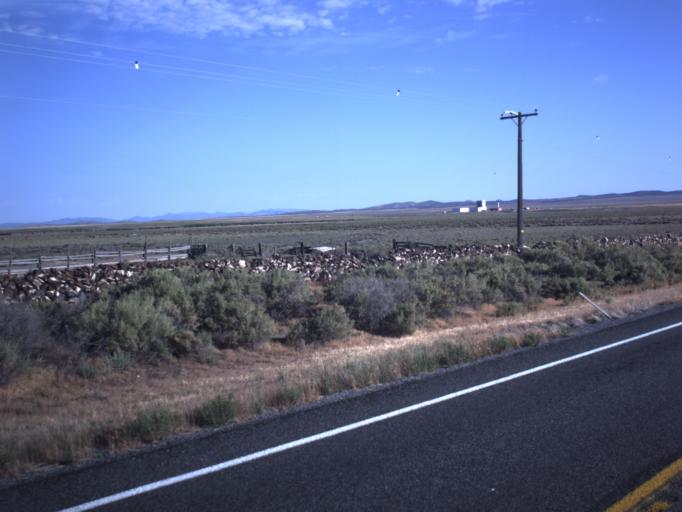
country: US
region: Utah
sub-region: Iron County
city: Enoch
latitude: 37.8593
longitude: -113.0316
